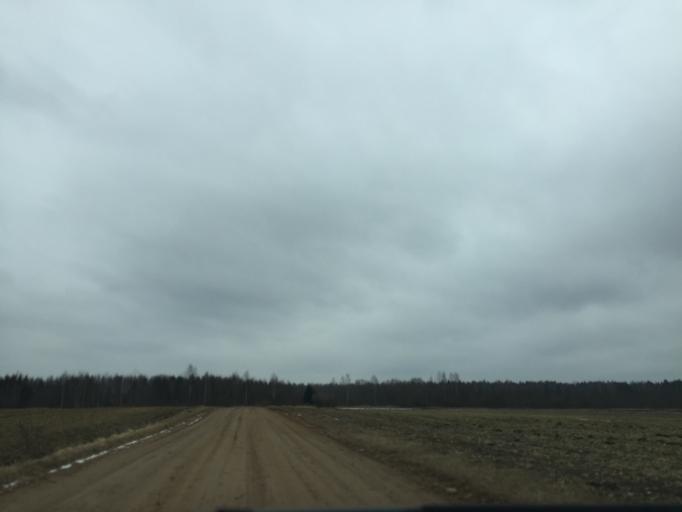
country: LV
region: Lielvarde
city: Lielvarde
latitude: 56.7576
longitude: 24.8120
